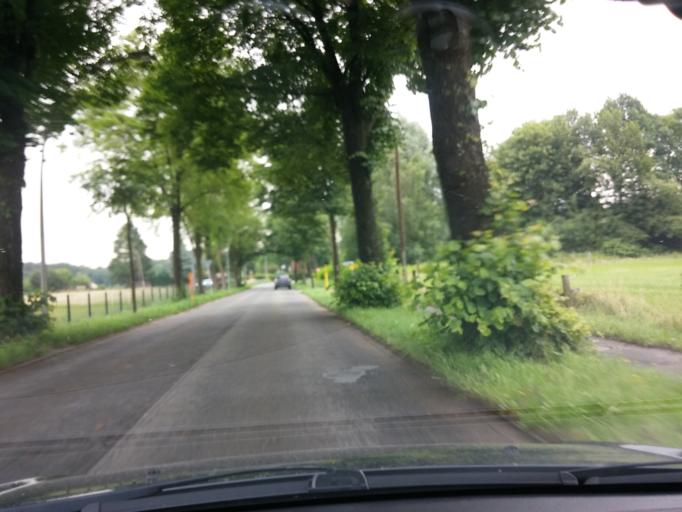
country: DE
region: North Rhine-Westphalia
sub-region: Regierungsbezirk Munster
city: Gladbeck
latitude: 51.6106
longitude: 6.9886
